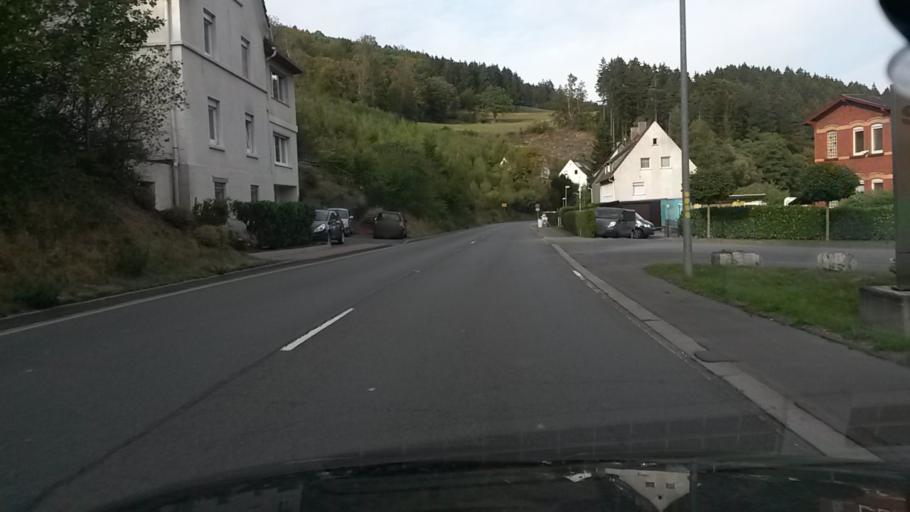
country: DE
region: North Rhine-Westphalia
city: Altena
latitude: 51.2354
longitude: 7.6981
